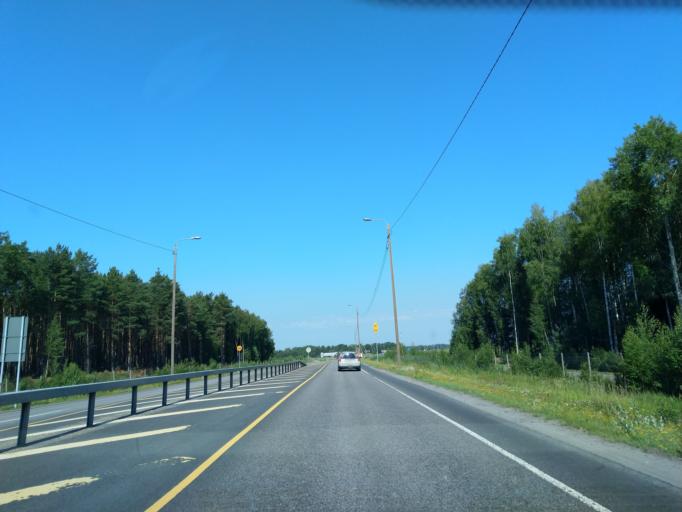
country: FI
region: Satakunta
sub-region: Pori
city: Nakkila
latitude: 61.3448
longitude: 22.0252
